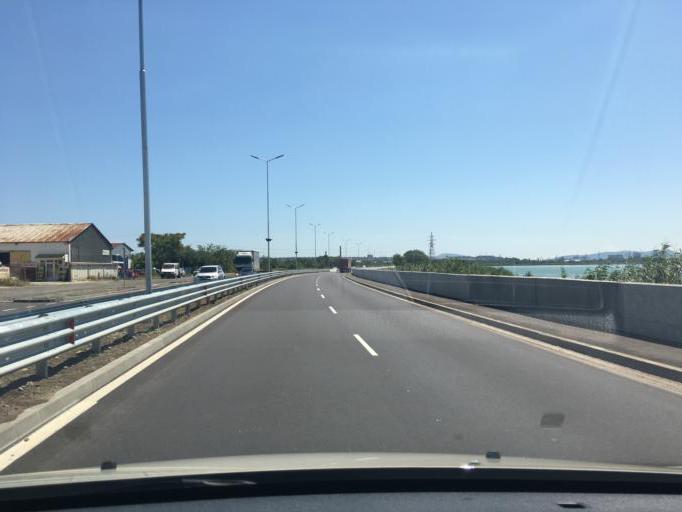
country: BG
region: Burgas
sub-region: Obshtina Burgas
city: Burgas
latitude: 42.5107
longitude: 27.4390
